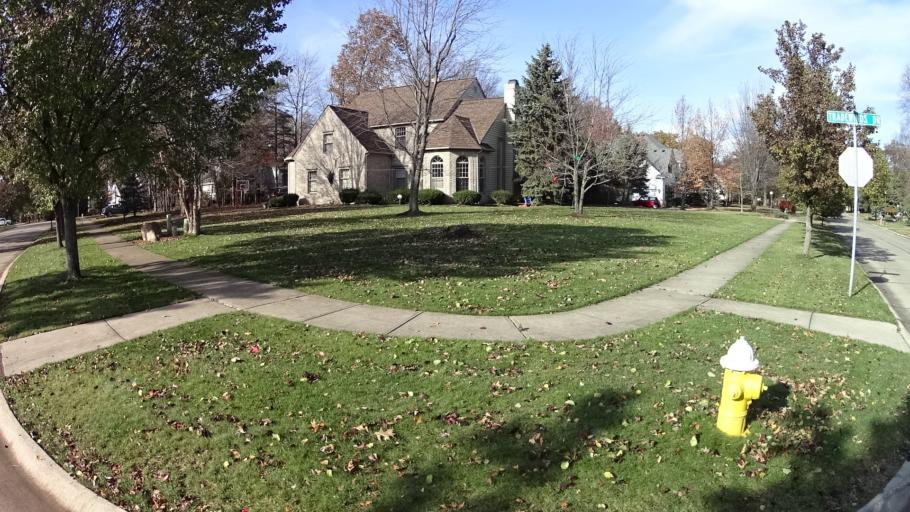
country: US
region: Ohio
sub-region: Cuyahoga County
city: Bay Village
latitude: 41.4984
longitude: -81.9721
